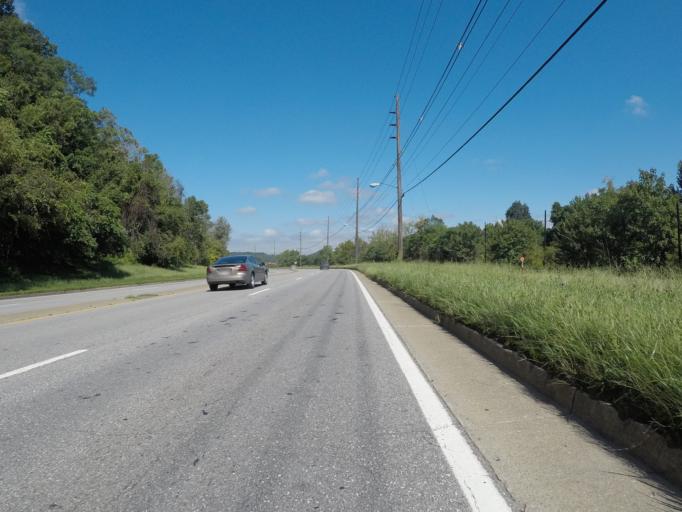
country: US
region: Kentucky
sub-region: Boyd County
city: Ashland
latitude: 38.4599
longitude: -82.6133
